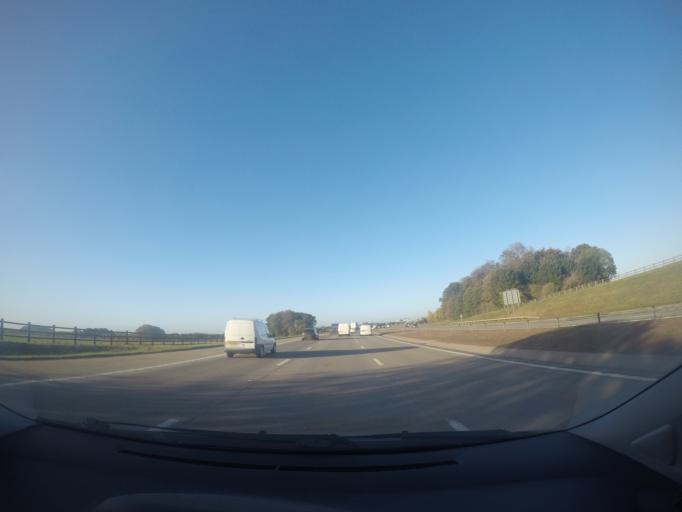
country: GB
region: England
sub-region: City and Borough of Leeds
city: Aberford
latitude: 53.8057
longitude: -1.3485
